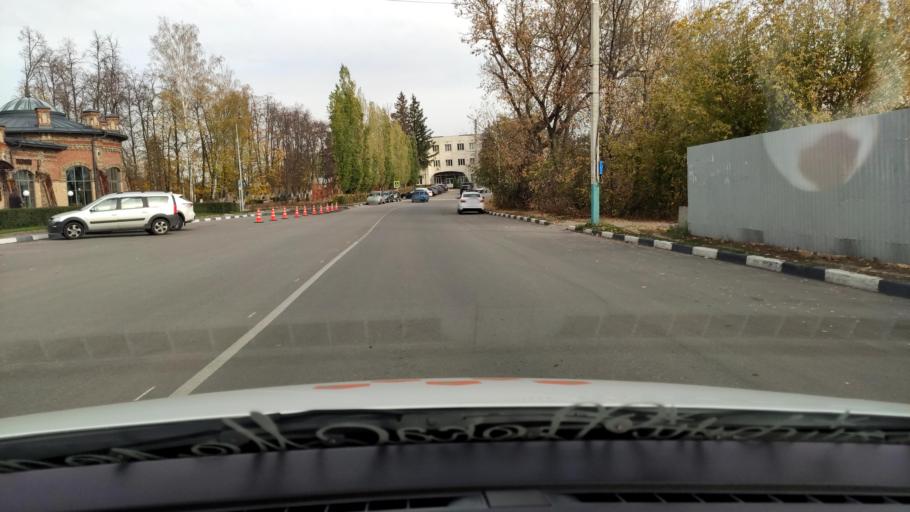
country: RU
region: Voronezj
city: Ramon'
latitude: 51.9133
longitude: 39.3392
